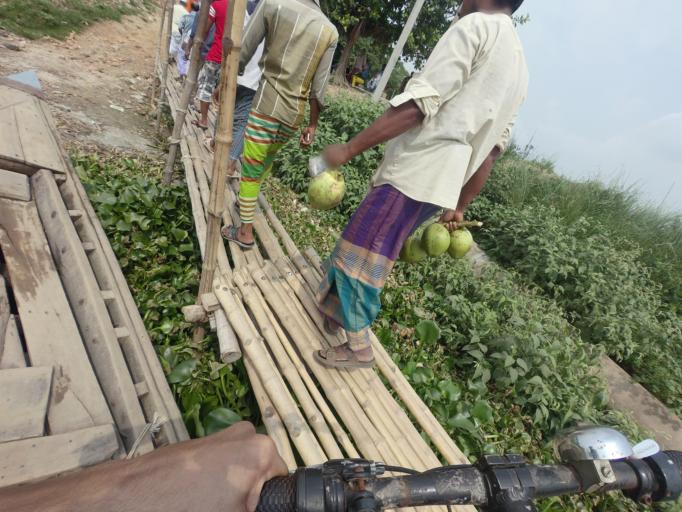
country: BD
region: Dhaka
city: Azimpur
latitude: 23.7322
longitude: 90.3524
